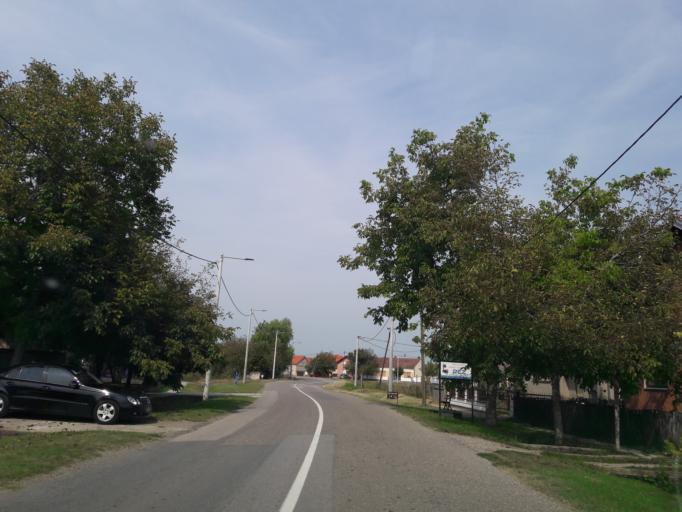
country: HR
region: Vukovarsko-Srijemska
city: Bobota
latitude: 45.4154
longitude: 18.8550
